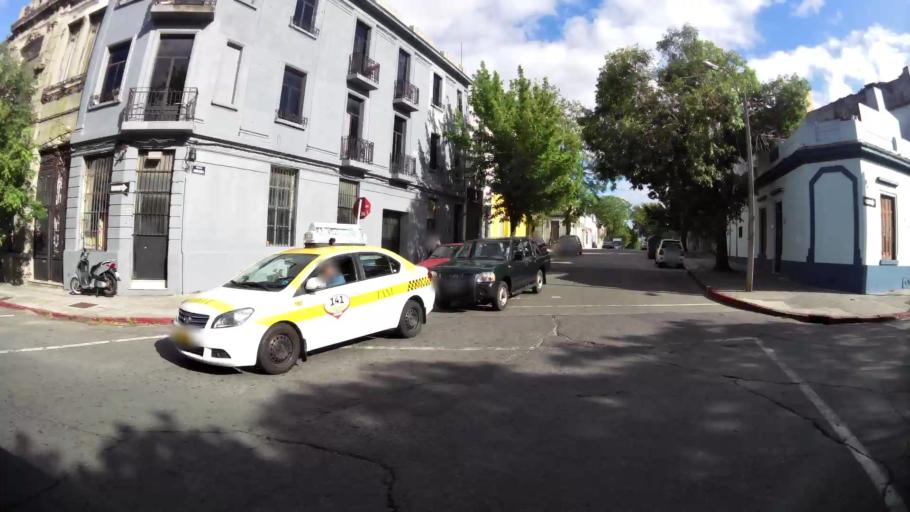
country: UY
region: Montevideo
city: Montevideo
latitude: -34.8929
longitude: -56.1763
